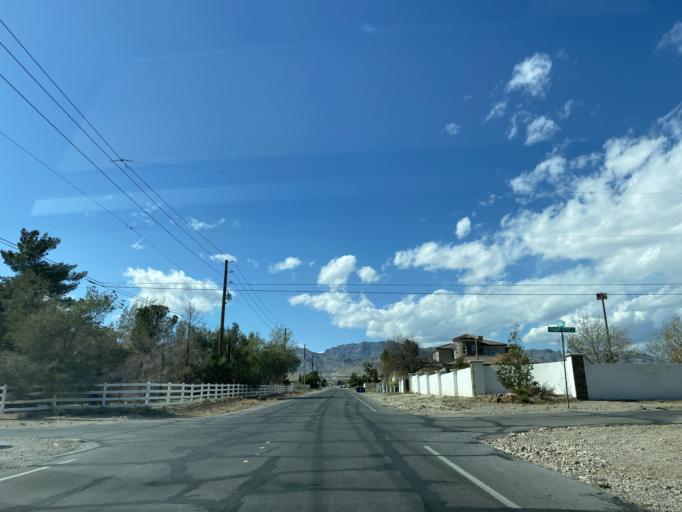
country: US
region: Nevada
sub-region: Clark County
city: Summerlin South
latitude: 36.2556
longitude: -115.2948
